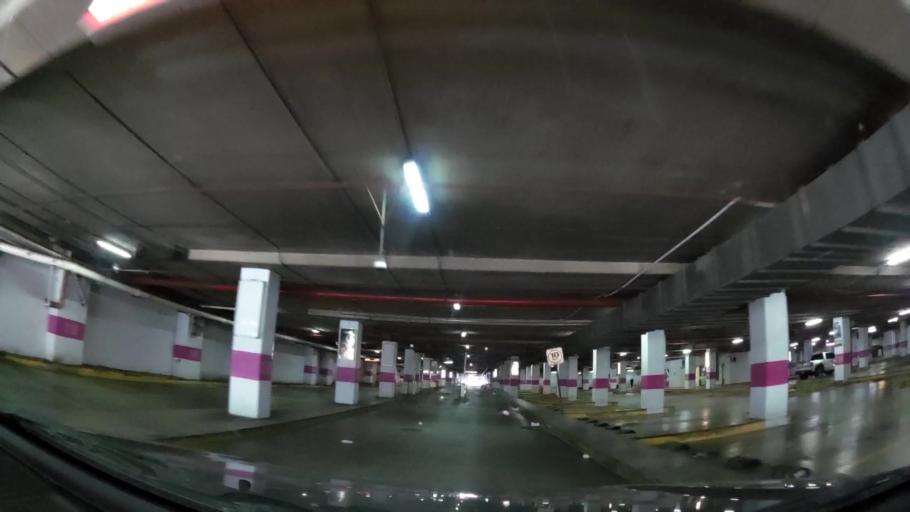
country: PA
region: Panama
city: Panama
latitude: 8.9756
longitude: -79.5176
